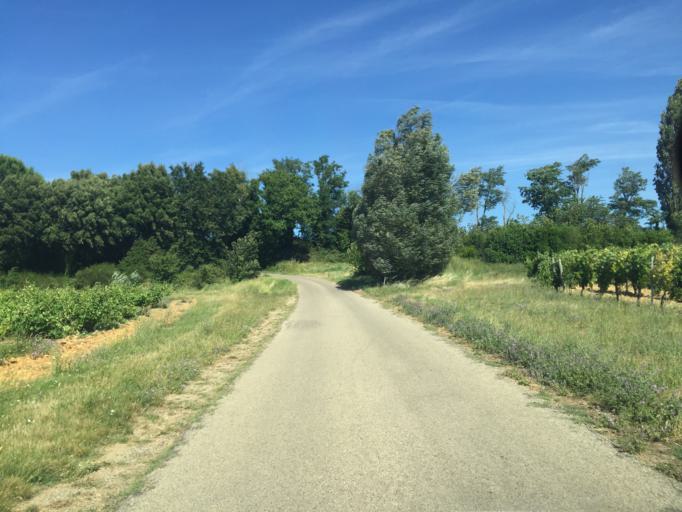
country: FR
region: Provence-Alpes-Cote d'Azur
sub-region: Departement du Vaucluse
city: Chateauneuf-du-Pape
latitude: 44.0793
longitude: 4.8101
